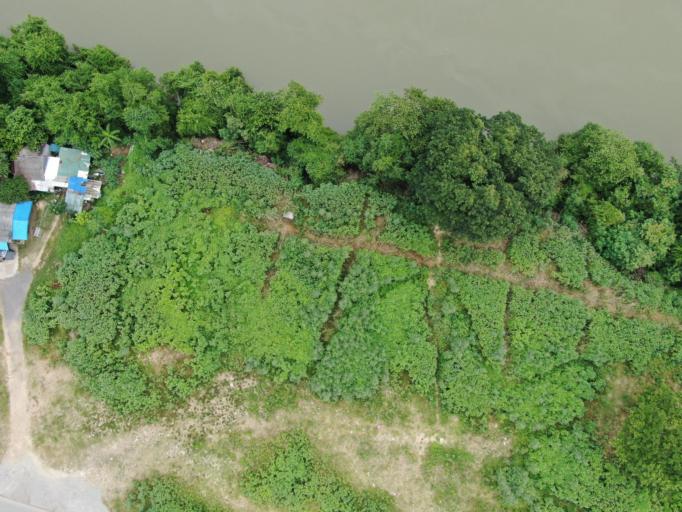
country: TH
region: Ratchaburi
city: Ban Pong
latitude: 13.8040
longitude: 99.8710
